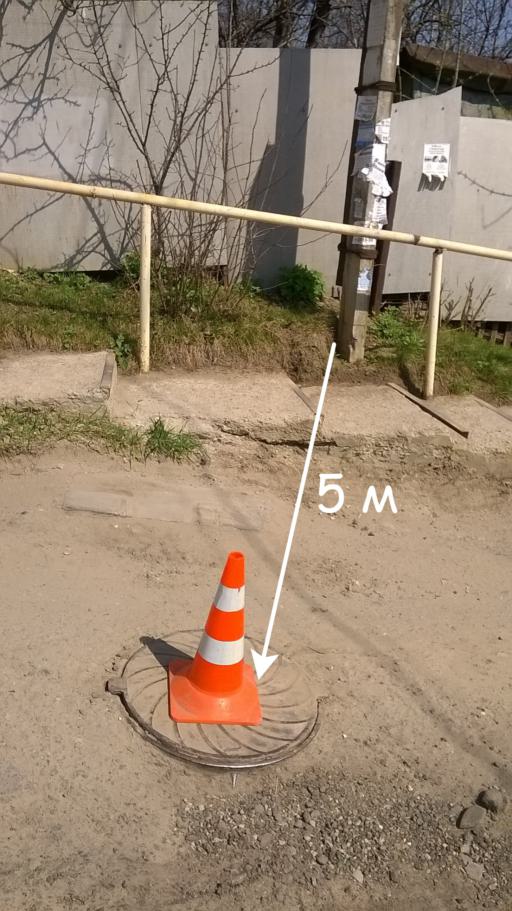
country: RU
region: Voronezj
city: Voronezh
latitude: 51.7089
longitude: 39.2315
